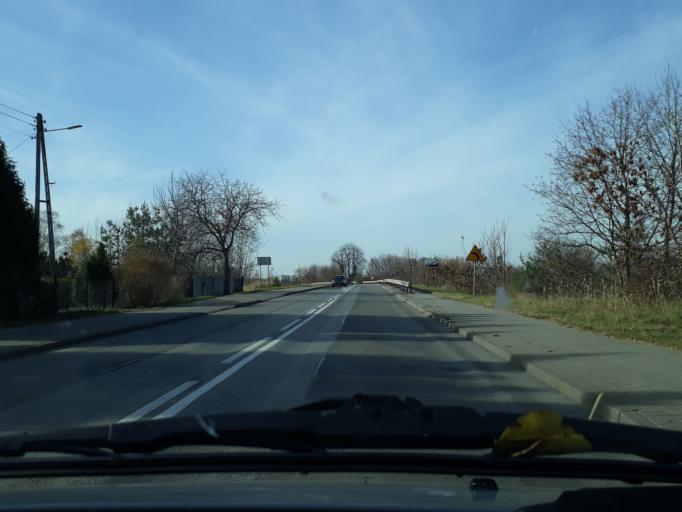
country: PL
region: Silesian Voivodeship
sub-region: Powiat myszkowski
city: Gniazdow
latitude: 50.5994
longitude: 19.1370
